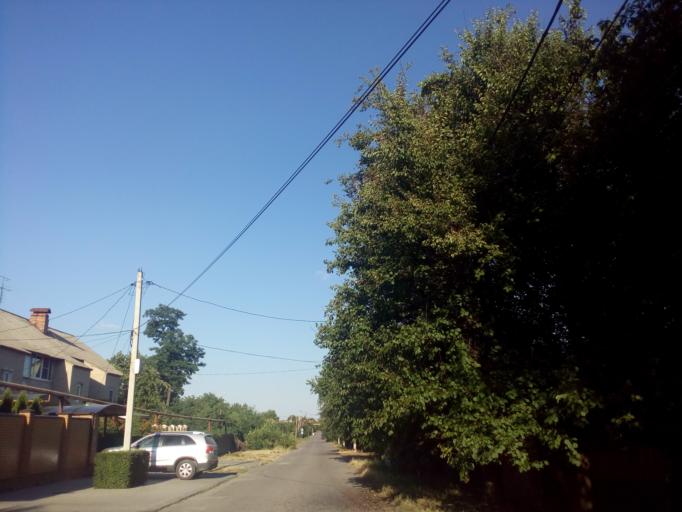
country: RU
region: Rostov
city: Sholokhovskiy
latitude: 48.2783
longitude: 41.0428
